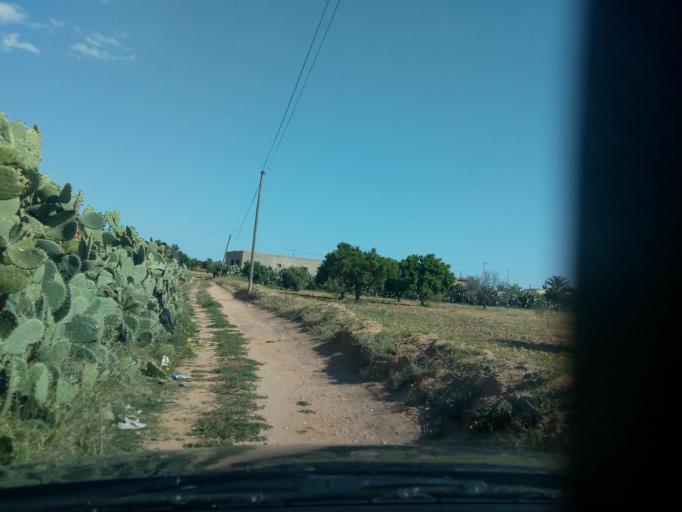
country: TN
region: Safaqis
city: Sfax
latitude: 34.7272
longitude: 10.6012
